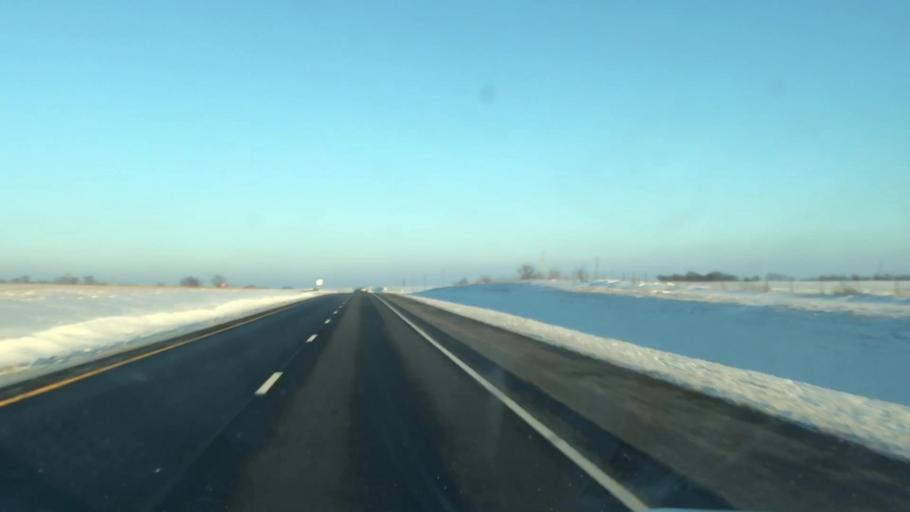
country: US
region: Missouri
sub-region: DeKalb County
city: Maysville
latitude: 39.7615
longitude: -94.3776
